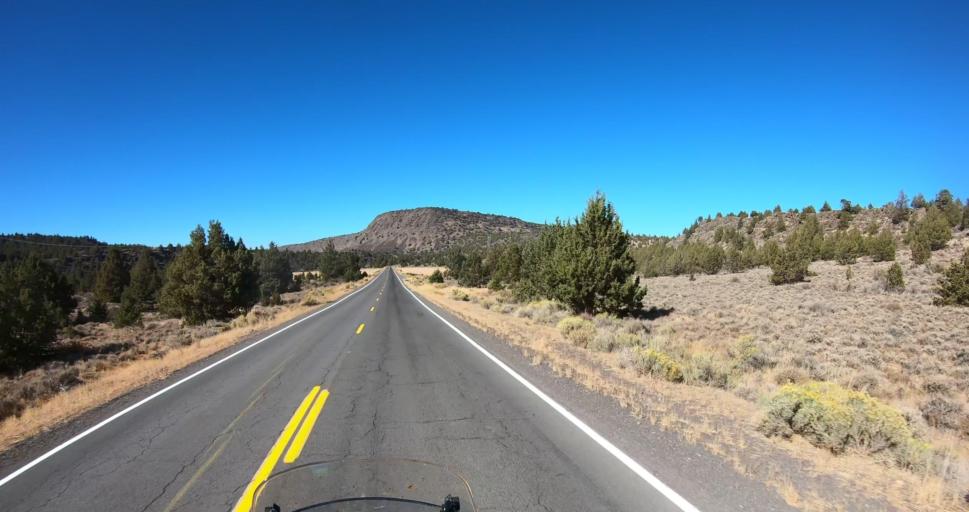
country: US
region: Oregon
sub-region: Deschutes County
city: La Pine
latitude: 43.0337
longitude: -120.7931
